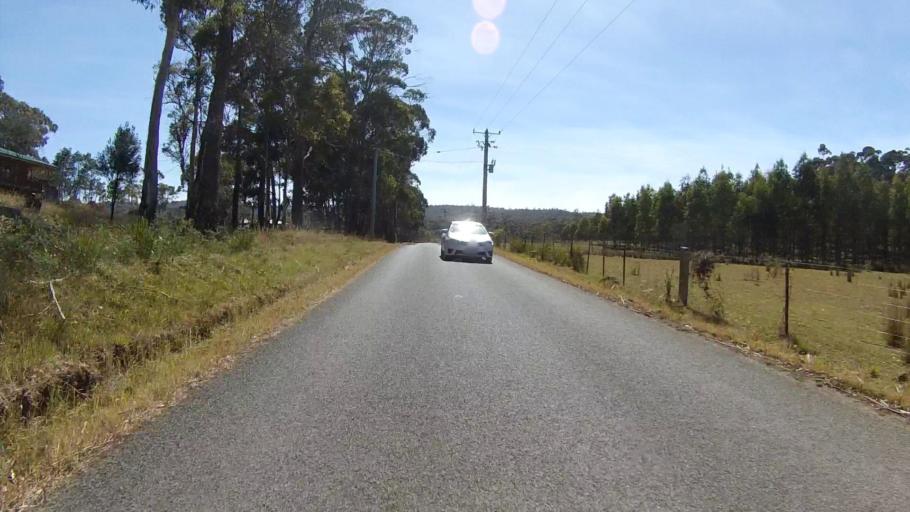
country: AU
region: Tasmania
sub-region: Sorell
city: Sorell
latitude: -42.7500
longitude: 147.7164
